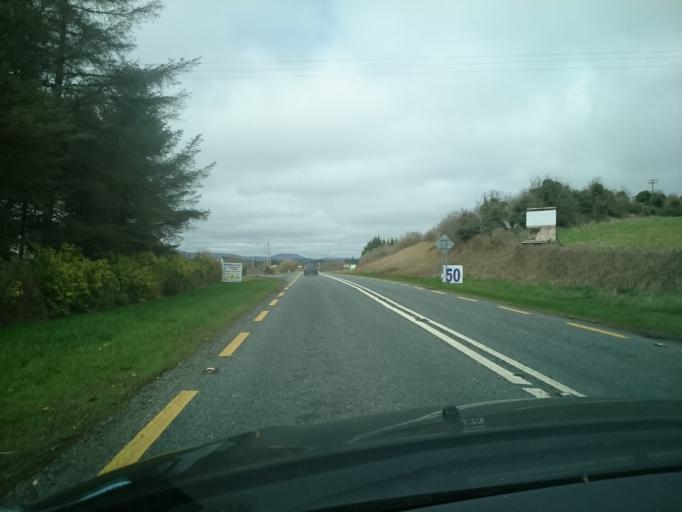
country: IE
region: Connaught
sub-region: Maigh Eo
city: Castlebar
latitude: 53.8340
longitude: -9.1862
